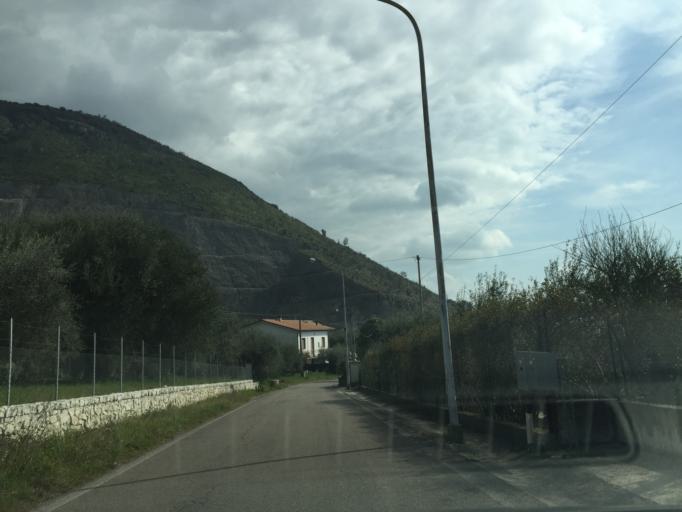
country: IT
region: Latium
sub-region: Provincia di Frosinone
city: Castrocielo
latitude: 41.5269
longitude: 13.7010
